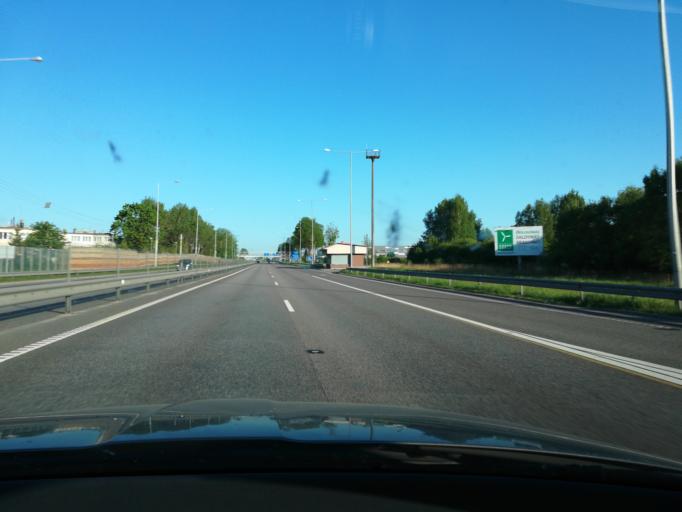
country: LT
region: Vilnius County
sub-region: Vilniaus Rajonas
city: Vievis
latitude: 54.7731
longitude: 24.8156
